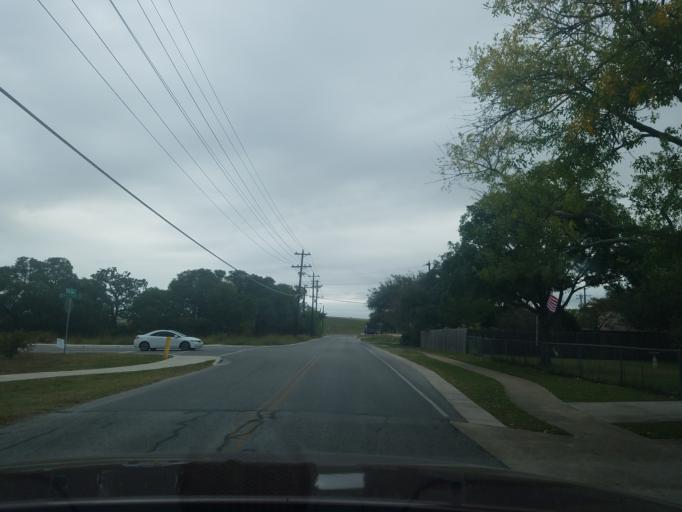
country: US
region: Texas
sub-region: Williamson County
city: Cedar Park
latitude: 30.4822
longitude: -97.8075
